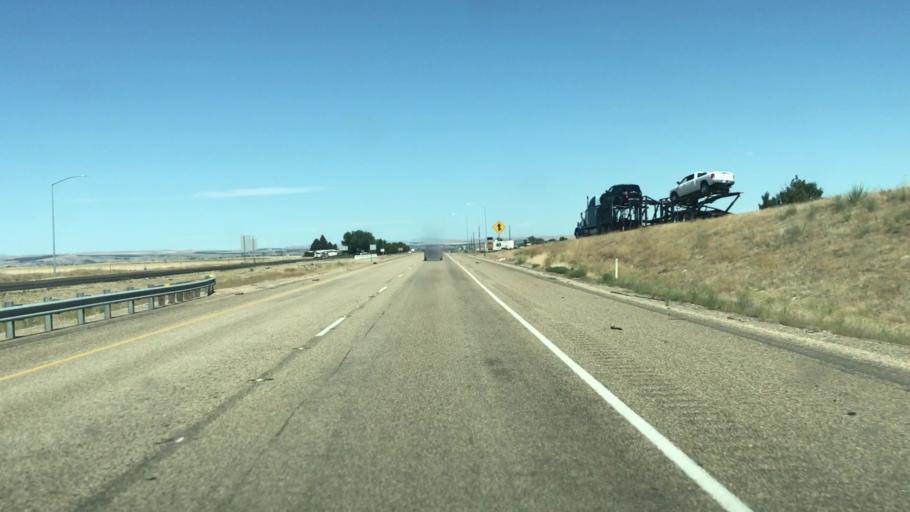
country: US
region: Idaho
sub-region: Payette County
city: Fruitland
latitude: 43.9723
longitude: -116.9150
